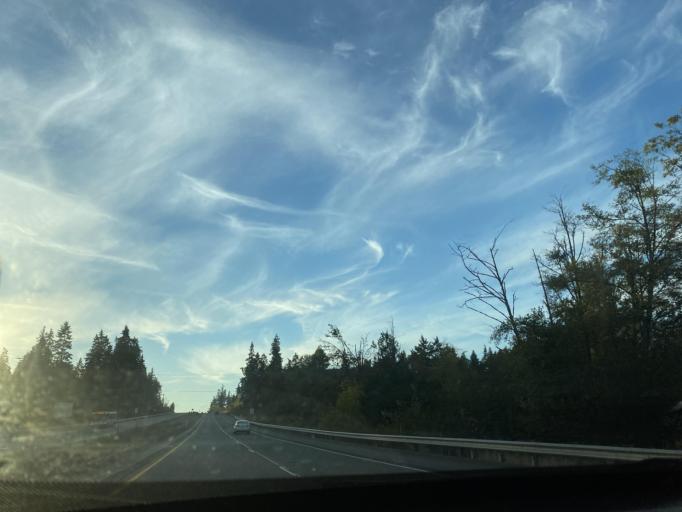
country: US
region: Washington
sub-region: Clallam County
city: Sequim
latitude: 48.0843
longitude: -123.2015
